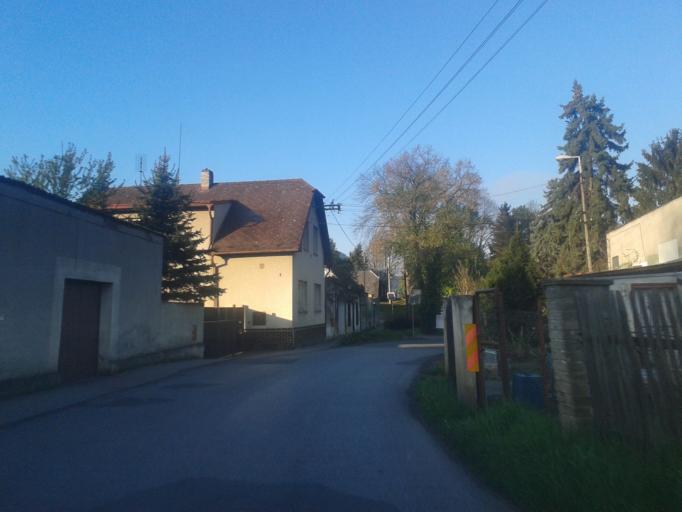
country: CZ
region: Central Bohemia
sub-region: Okres Beroun
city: Kraluv Dvur
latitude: 49.9295
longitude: 14.0199
